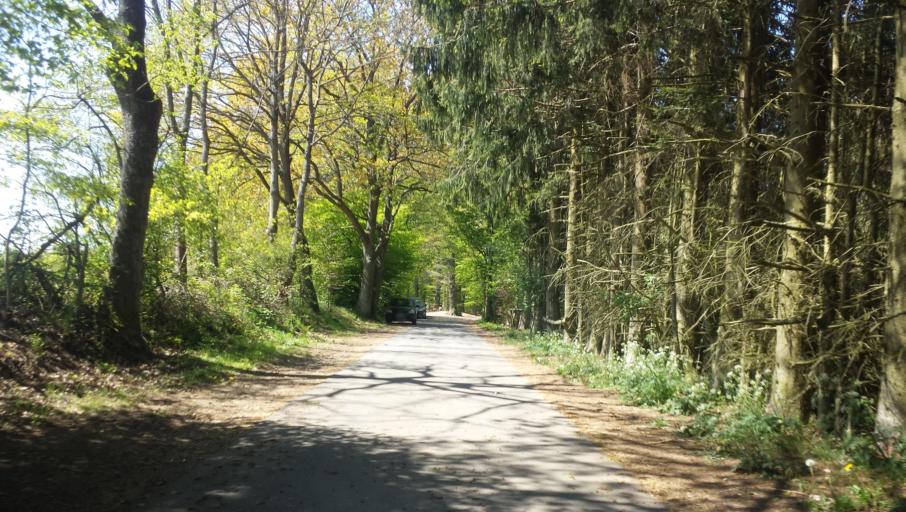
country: DE
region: Rheinland-Pfalz
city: Winnweiler
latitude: 49.5654
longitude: 7.8332
